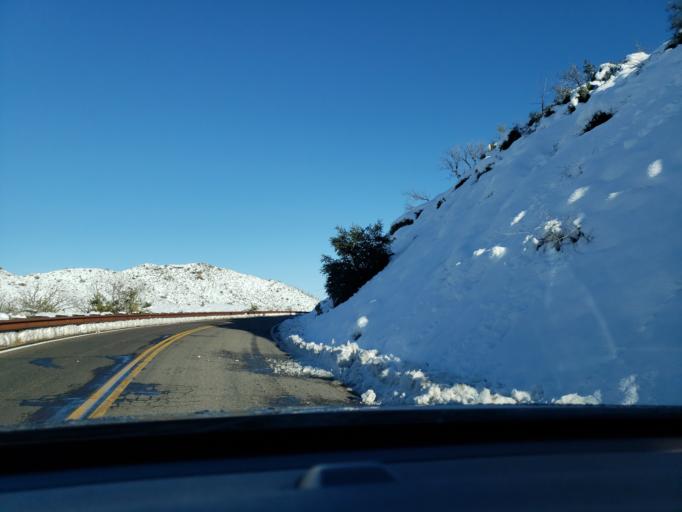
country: US
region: Arizona
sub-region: Maricopa County
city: Carefree
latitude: 33.8956
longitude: -111.8192
